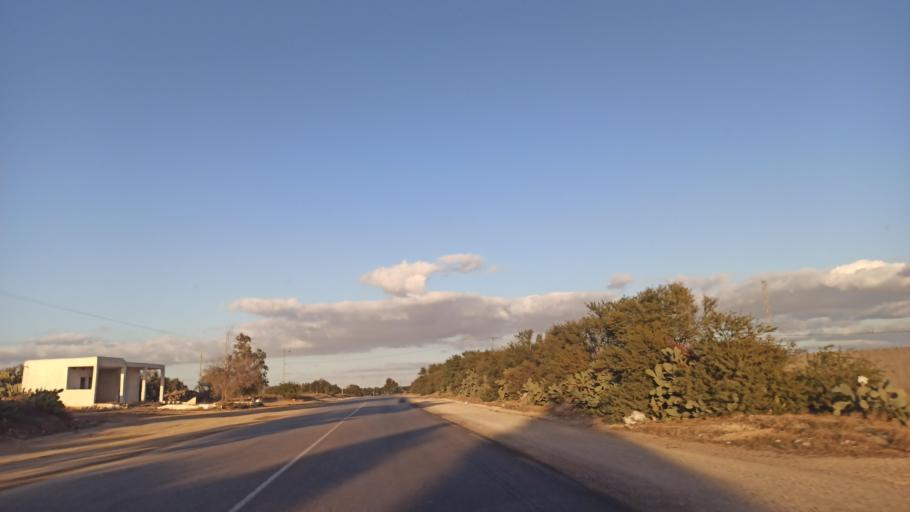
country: TN
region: Al Qayrawan
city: Sbikha
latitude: 35.8737
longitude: 10.2197
